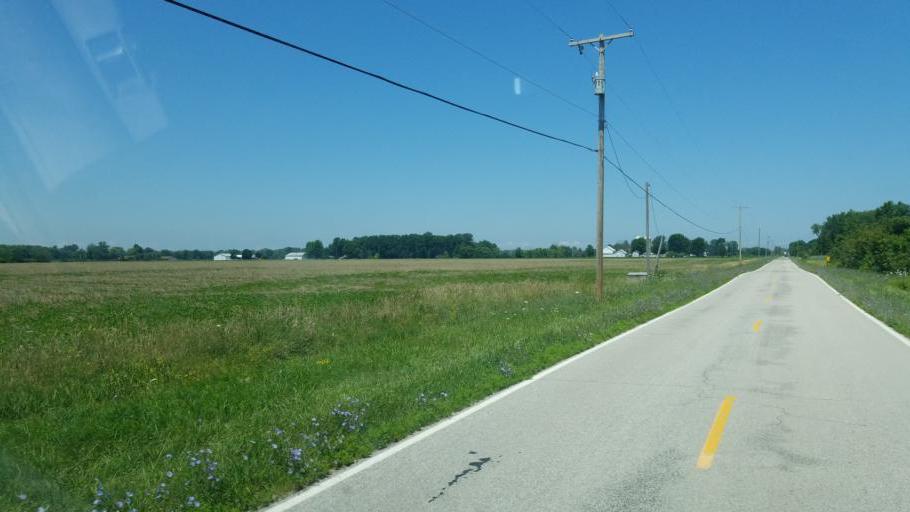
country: US
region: Ohio
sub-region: Sandusky County
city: Clyde
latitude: 41.4091
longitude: -83.0116
